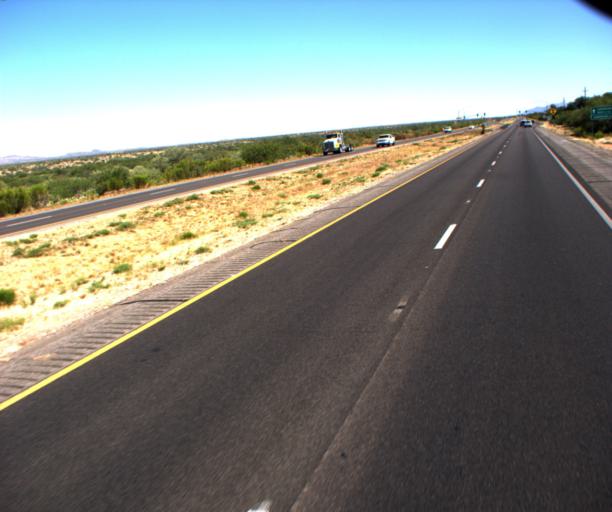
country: US
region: Arizona
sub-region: Pima County
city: Catalina
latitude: 32.5209
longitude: -110.9273
